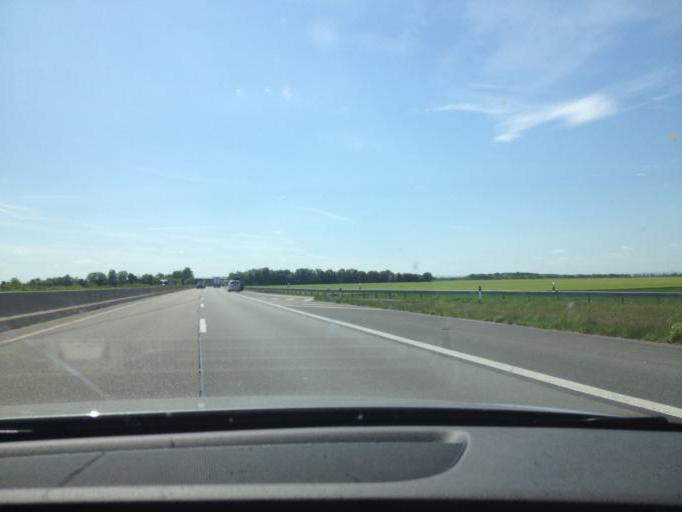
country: DE
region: North Rhine-Westphalia
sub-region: Regierungsbezirk Koln
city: Weilerswist
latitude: 50.7509
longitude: 6.8104
